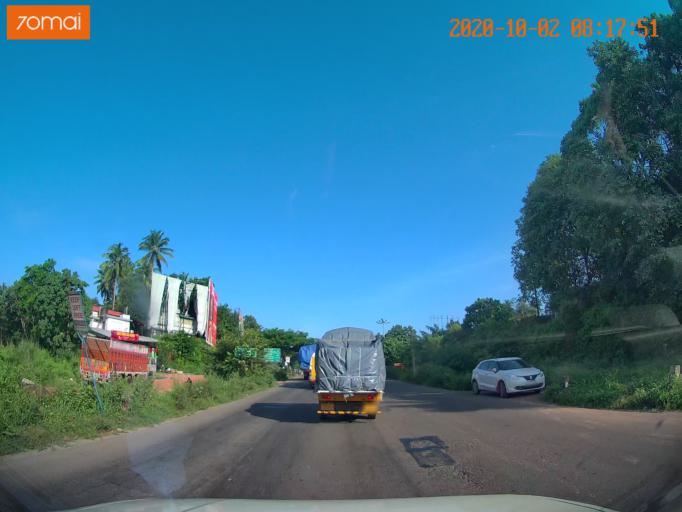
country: IN
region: Kerala
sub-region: Kozhikode
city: Kozhikode
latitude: 11.3003
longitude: 75.7933
